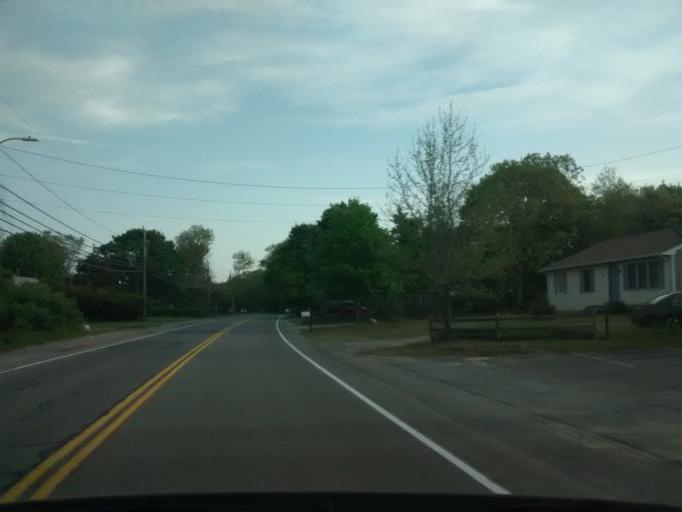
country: US
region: Massachusetts
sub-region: Barnstable County
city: Teaticket
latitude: 41.5753
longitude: -70.5935
